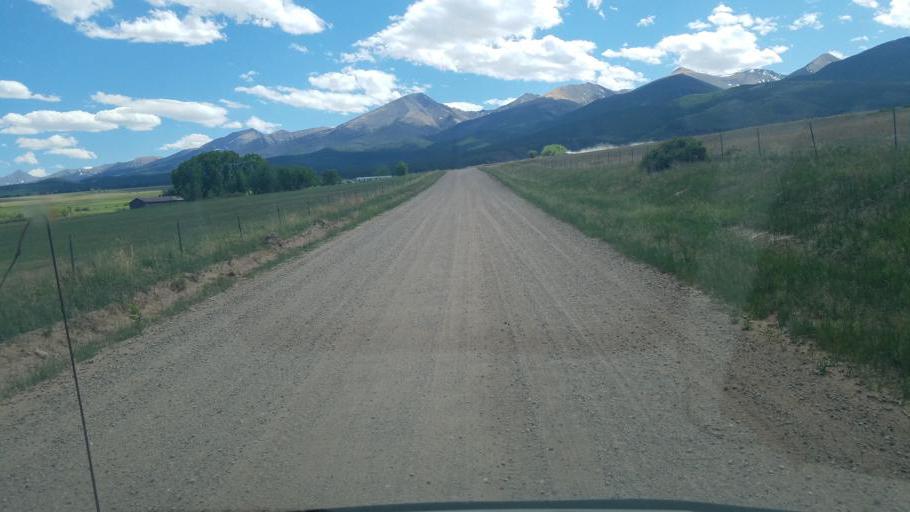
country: US
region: Colorado
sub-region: Custer County
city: Westcliffe
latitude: 38.2614
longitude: -105.6132
